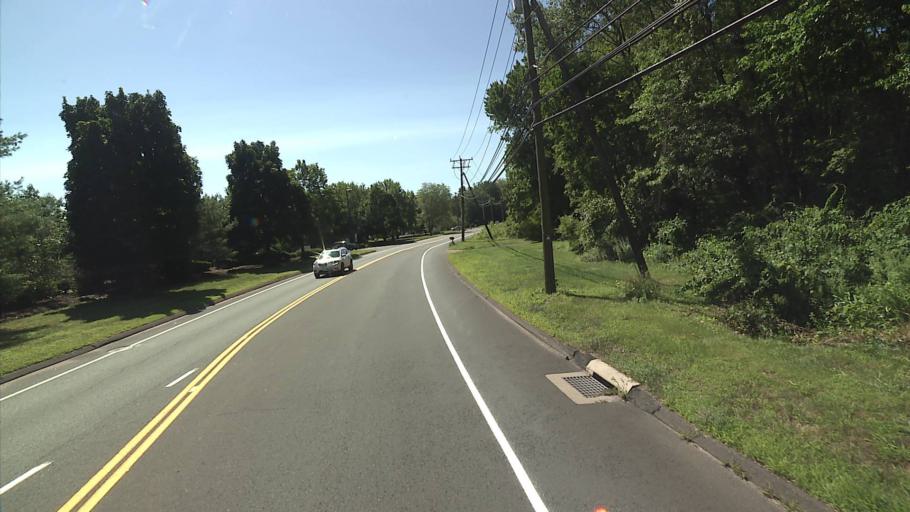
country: US
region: Connecticut
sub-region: Hartford County
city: Salmon Brook
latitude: 41.9355
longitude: -72.7908
